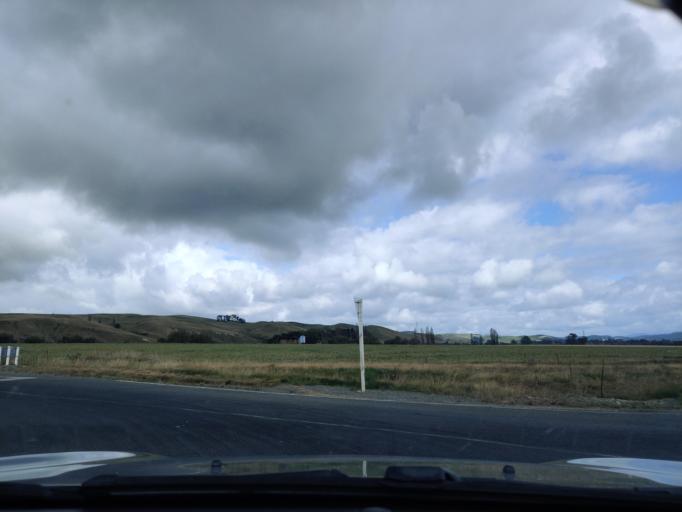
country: NZ
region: Canterbury
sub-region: Hurunui District
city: Amberley
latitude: -43.1276
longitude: 172.6816
